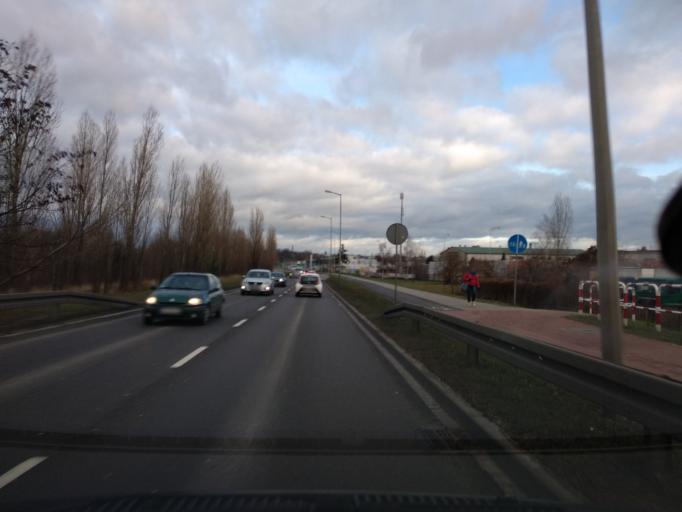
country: PL
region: Greater Poland Voivodeship
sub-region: Kalisz
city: Kalisz
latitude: 51.7679
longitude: 18.0673
